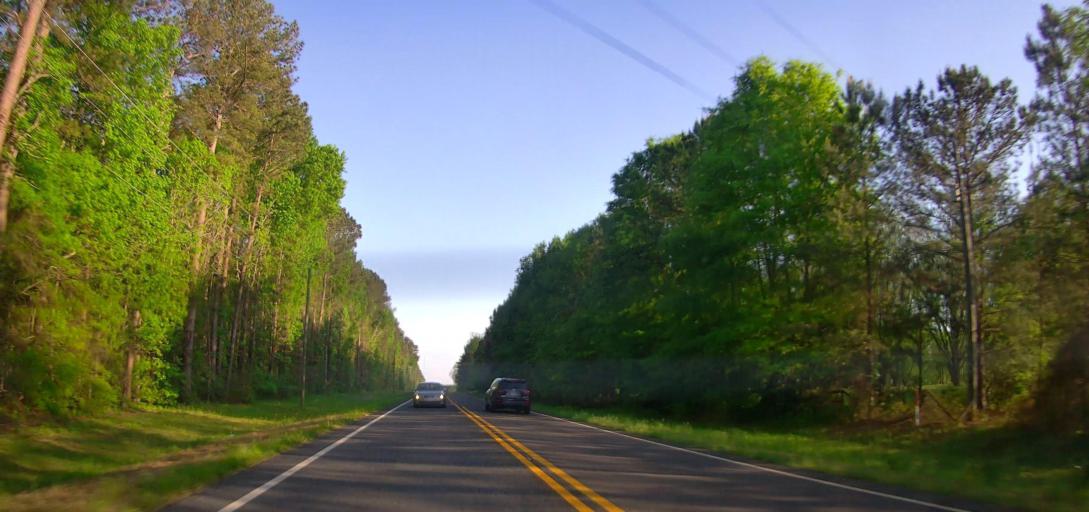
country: US
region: Georgia
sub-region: Jasper County
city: Monticello
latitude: 33.4590
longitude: -83.6324
